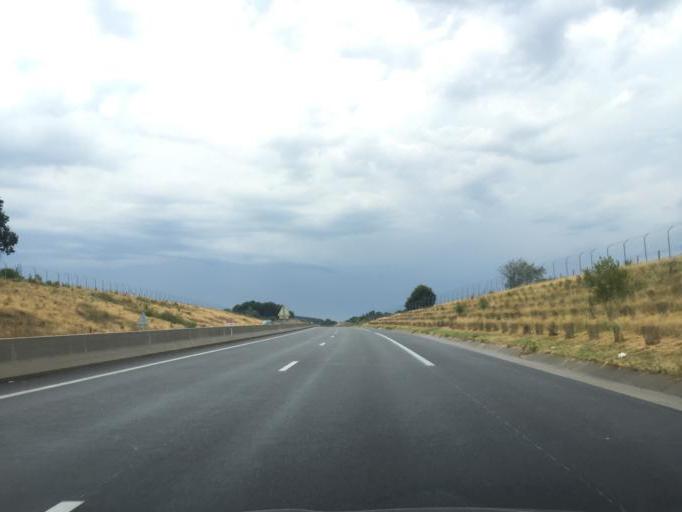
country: FR
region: Auvergne
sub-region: Departement de l'Allier
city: Lapalisse
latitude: 46.2173
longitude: 3.7017
